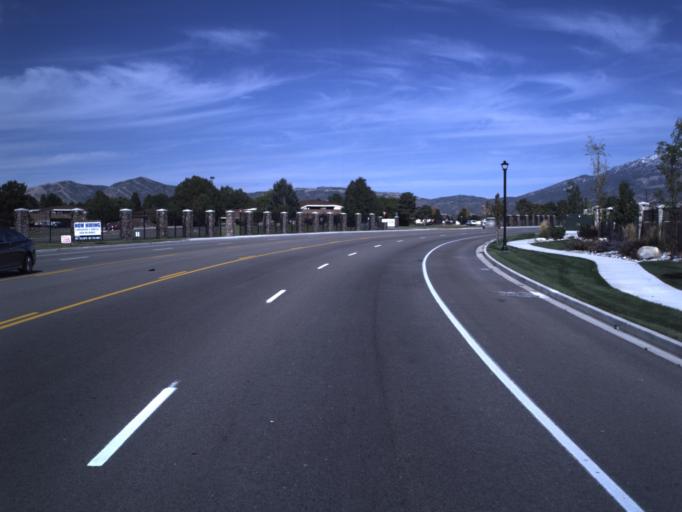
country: US
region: Utah
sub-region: Utah County
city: Cedar Hills
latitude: 40.3963
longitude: -111.7727
